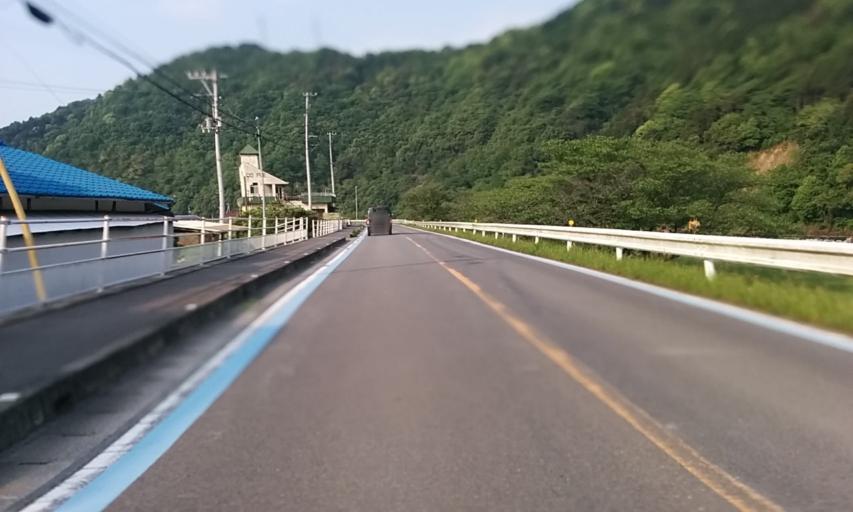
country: JP
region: Ehime
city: Saijo
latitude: 33.8914
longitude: 133.1923
